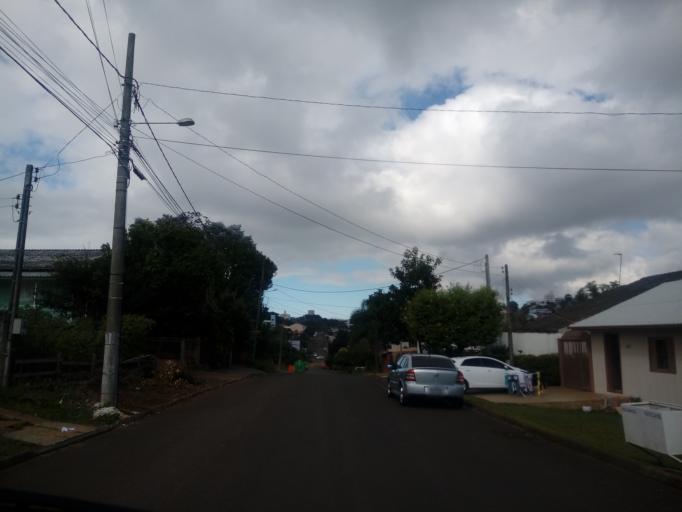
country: BR
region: Santa Catarina
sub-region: Chapeco
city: Chapeco
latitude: -27.1137
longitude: -52.6203
